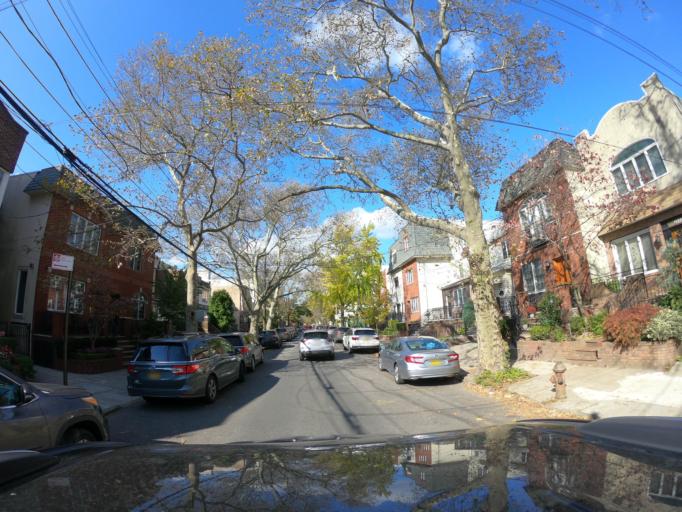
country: US
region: New York
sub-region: Kings County
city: Bensonhurst
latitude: 40.6241
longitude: -73.9800
